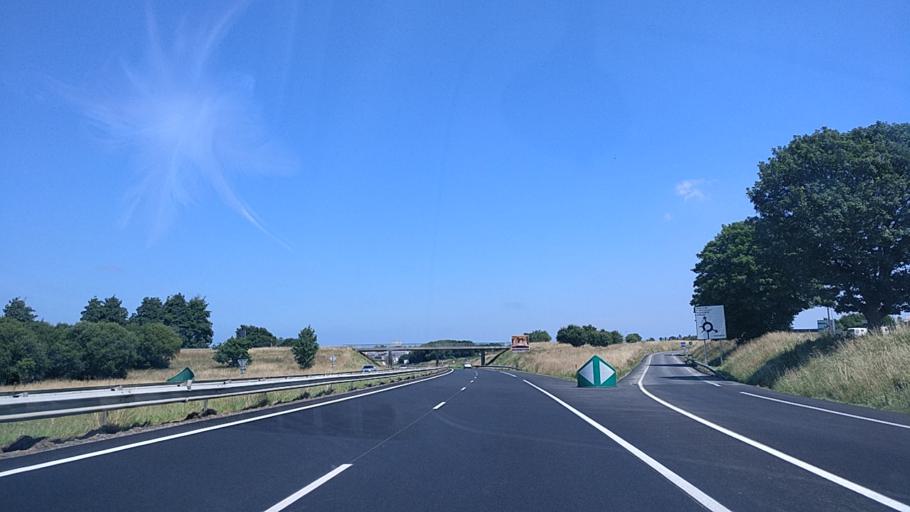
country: FR
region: Brittany
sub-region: Departement des Cotes-d'Armor
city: Tremuson
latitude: 48.5226
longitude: -2.8765
